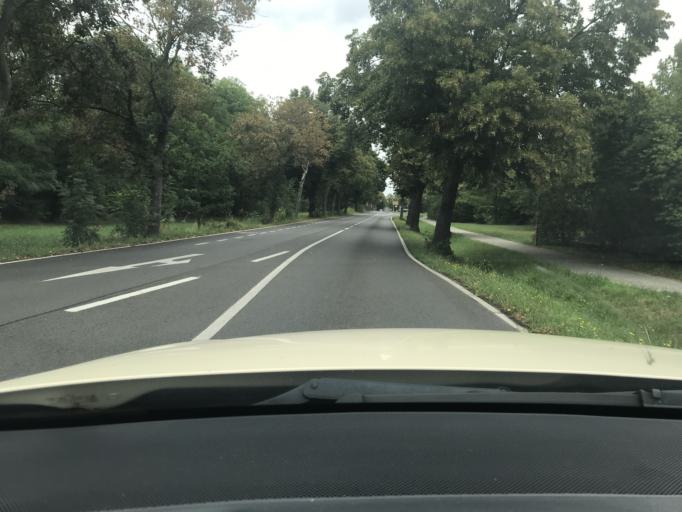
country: DE
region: Saxony
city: Markkleeberg
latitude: 51.2713
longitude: 12.3542
